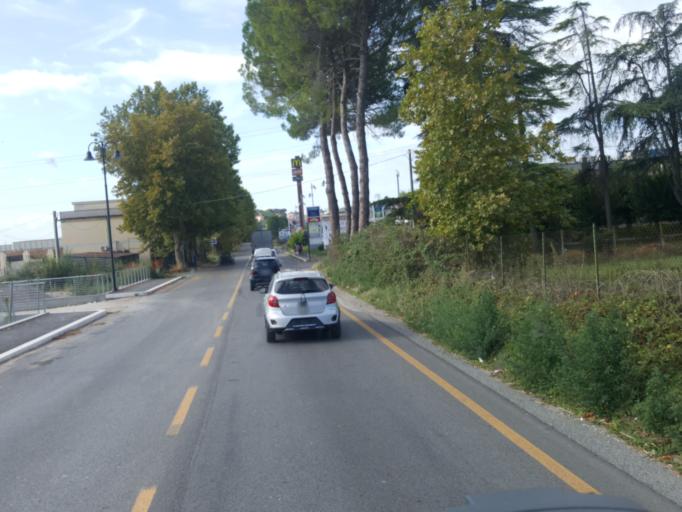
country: IT
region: Latium
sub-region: Citta metropolitana di Roma Capitale
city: Bivio di Capanelle
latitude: 42.1160
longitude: 12.5881
